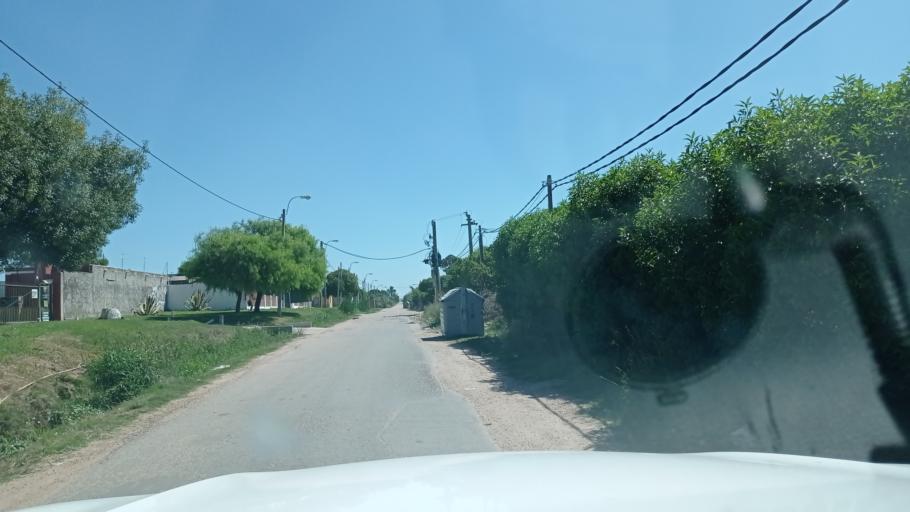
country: UY
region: Montevideo
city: Montevideo
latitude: -34.8689
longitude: -56.2712
